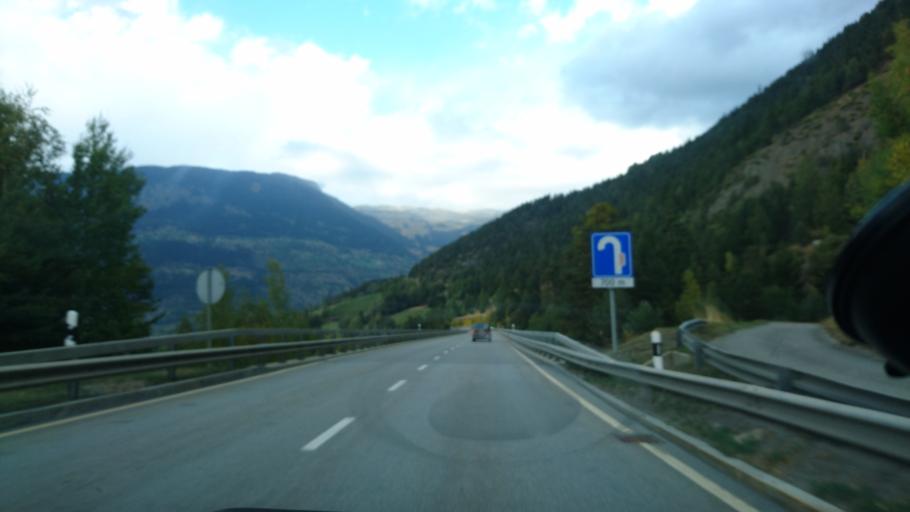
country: CH
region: Valais
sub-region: Brig District
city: Naters
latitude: 46.3219
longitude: 8.0333
